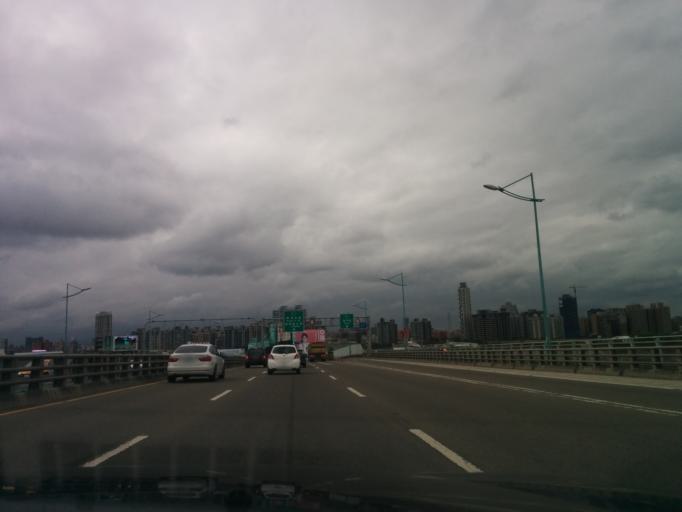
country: TW
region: Taipei
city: Taipei
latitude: 25.0977
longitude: 121.4977
